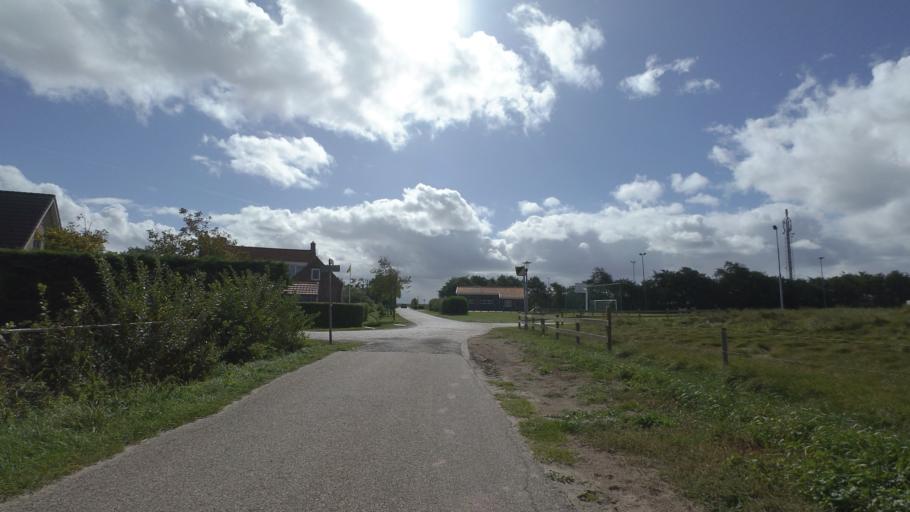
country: NL
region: Friesland
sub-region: Gemeente Ameland
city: Nes
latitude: 53.4489
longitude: 5.7935
